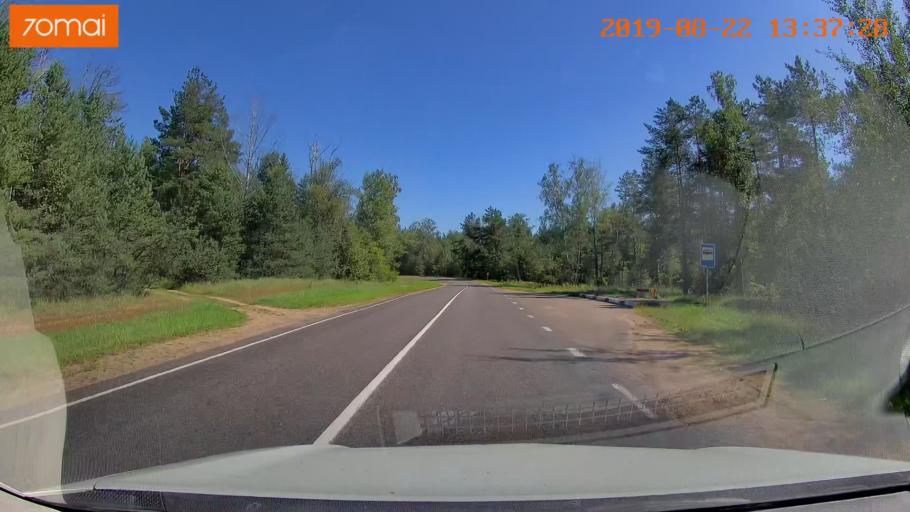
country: BY
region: Minsk
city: Staryya Darohi
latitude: 53.2166
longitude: 28.3000
